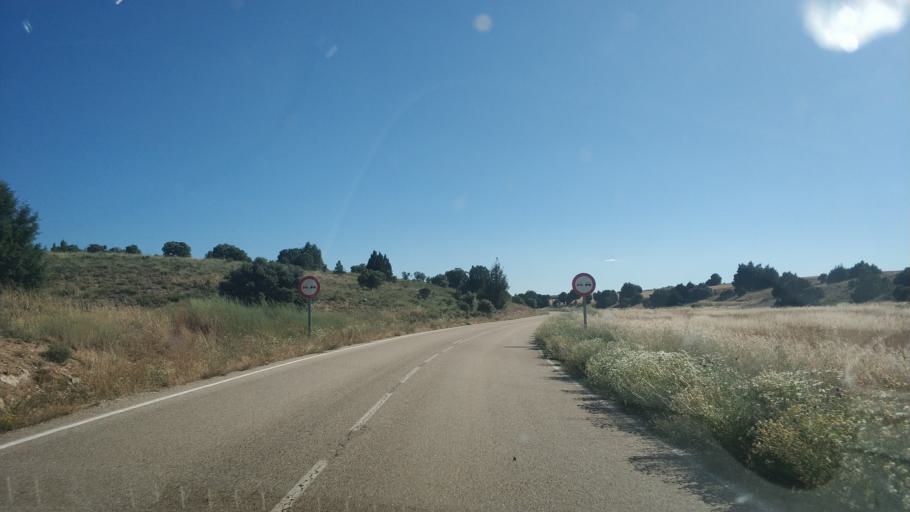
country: ES
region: Castille and Leon
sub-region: Provincia de Soria
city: San Esteban de Gormaz
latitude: 41.4912
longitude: -3.2051
